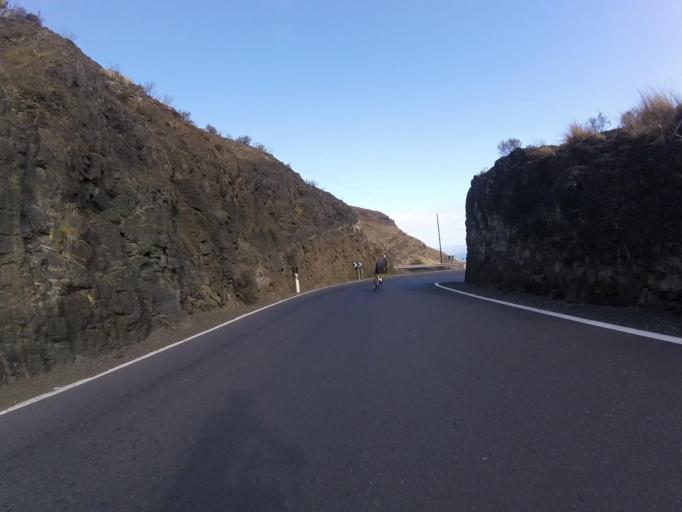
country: ES
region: Canary Islands
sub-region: Provincia de Las Palmas
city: Agaete
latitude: 28.0793
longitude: -15.7074
